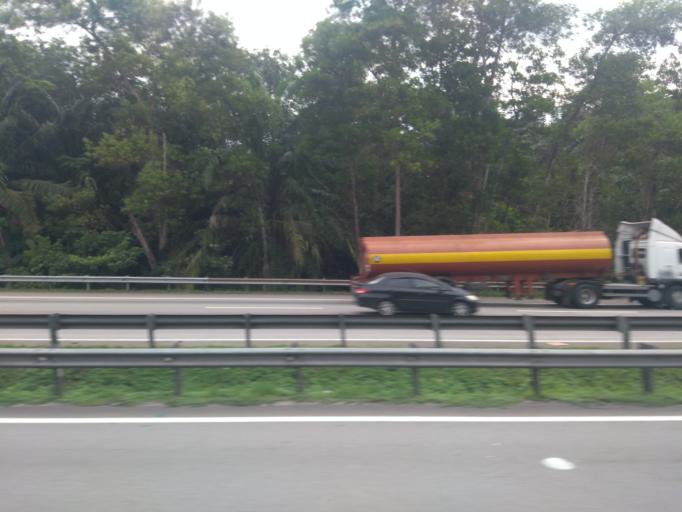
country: MY
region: Negeri Sembilan
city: Seremban
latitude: 2.6530
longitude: 101.9907
